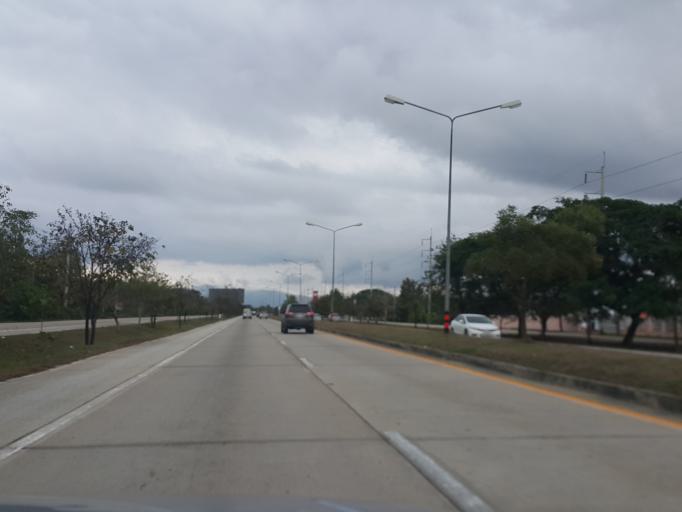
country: TH
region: Lampang
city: Lampang
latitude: 18.2898
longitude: 99.4362
